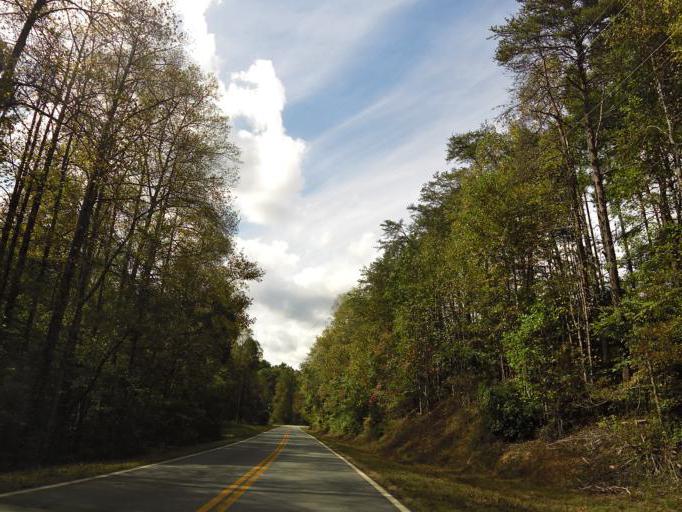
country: US
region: Georgia
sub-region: Pickens County
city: Jasper
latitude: 34.5250
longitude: -84.2719
